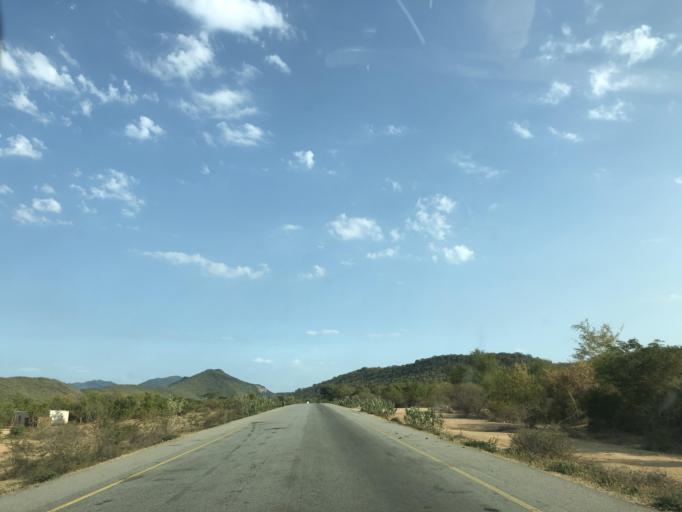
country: AO
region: Benguela
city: Benguela
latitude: -13.2534
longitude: 13.7806
